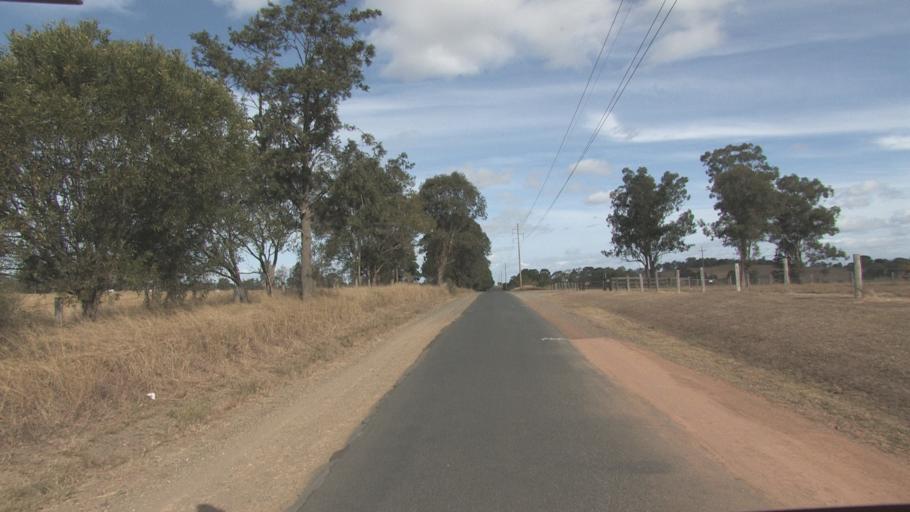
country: AU
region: Queensland
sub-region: Logan
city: Cedar Vale
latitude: -27.9152
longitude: 153.0137
